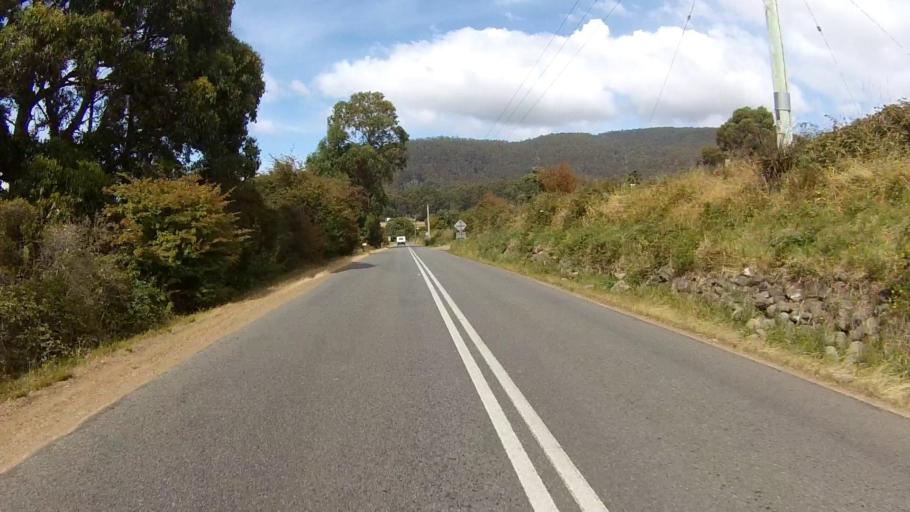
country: AU
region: Tasmania
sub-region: Kingborough
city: Kettering
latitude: -43.2119
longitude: 147.2563
